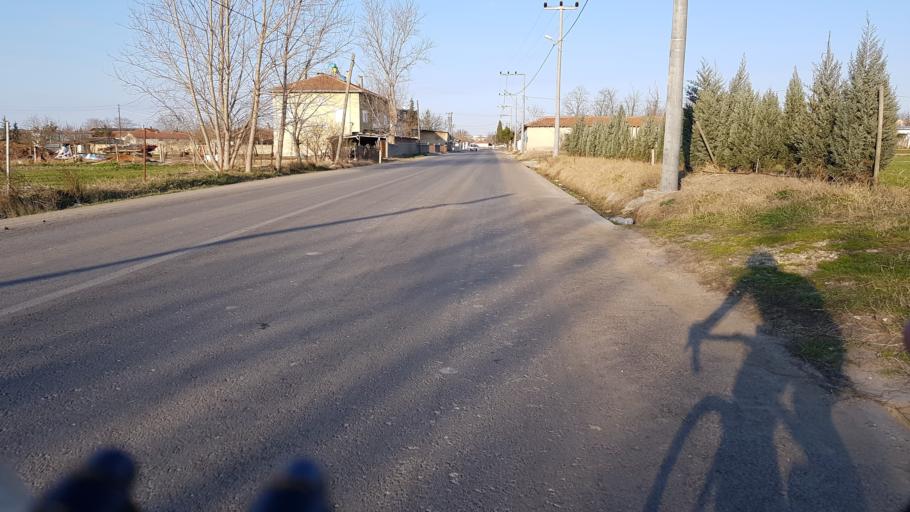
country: TR
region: Tekirdag
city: Beyazkoy
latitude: 41.3009
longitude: 27.7800
